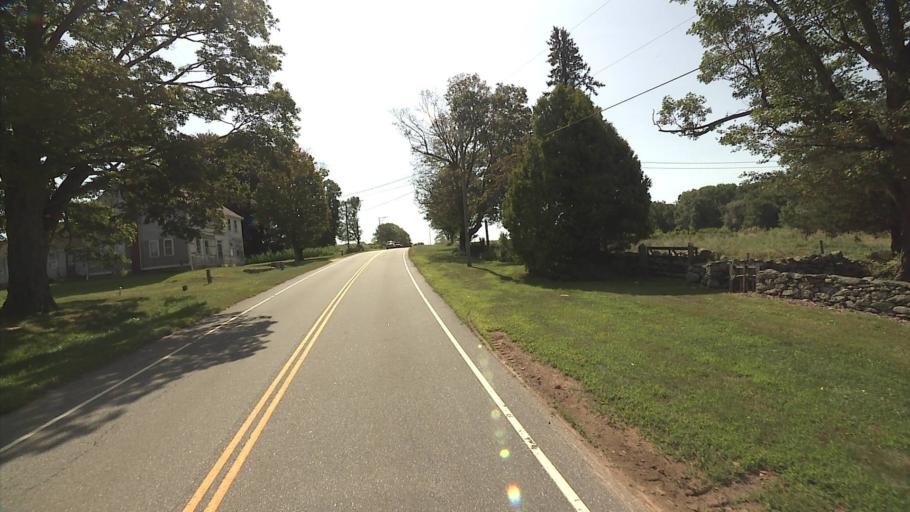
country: US
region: Connecticut
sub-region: Tolland County
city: Hebron
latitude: 41.6364
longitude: -72.3250
